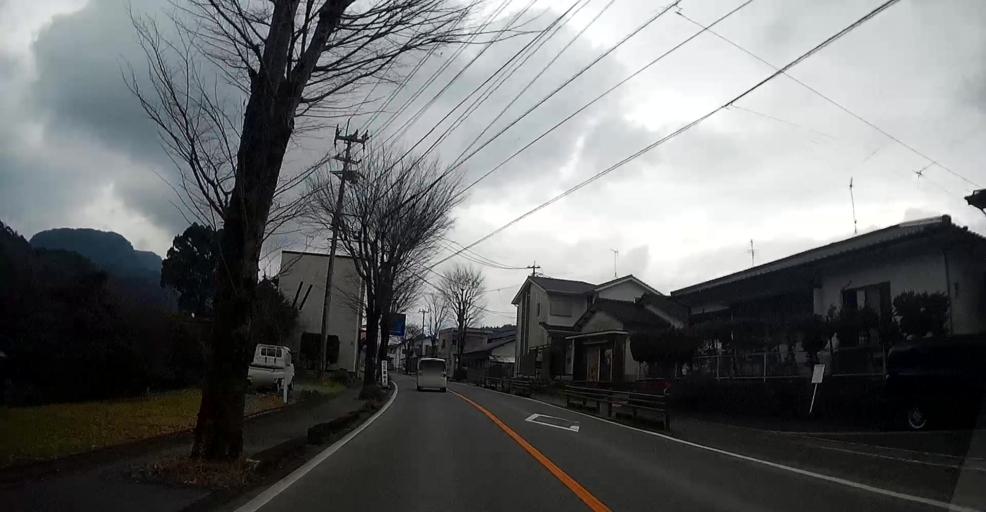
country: JP
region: Kumamoto
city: Matsubase
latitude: 32.6225
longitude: 130.8186
